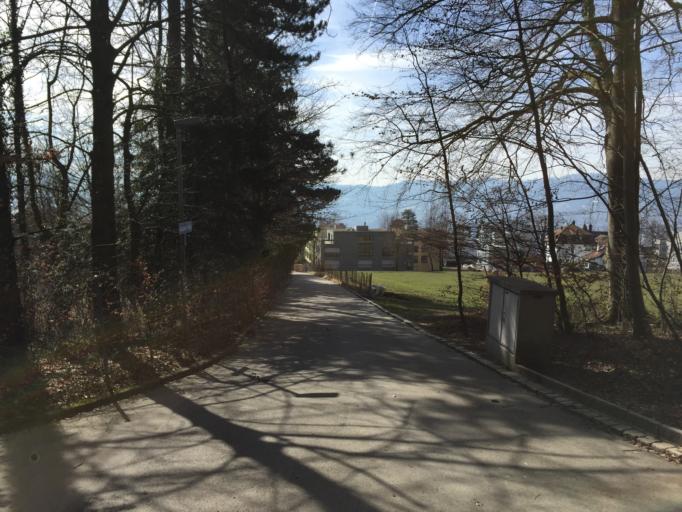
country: CH
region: Zurich
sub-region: Bezirk Zuerich
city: Zuerich (Kreis 7) / Fluntern
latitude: 47.3832
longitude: 8.5660
